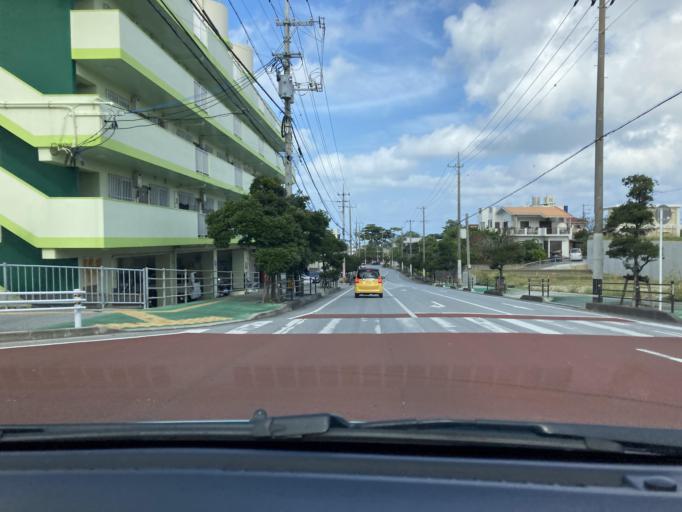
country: JP
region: Okinawa
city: Ginowan
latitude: 26.2623
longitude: 127.7505
